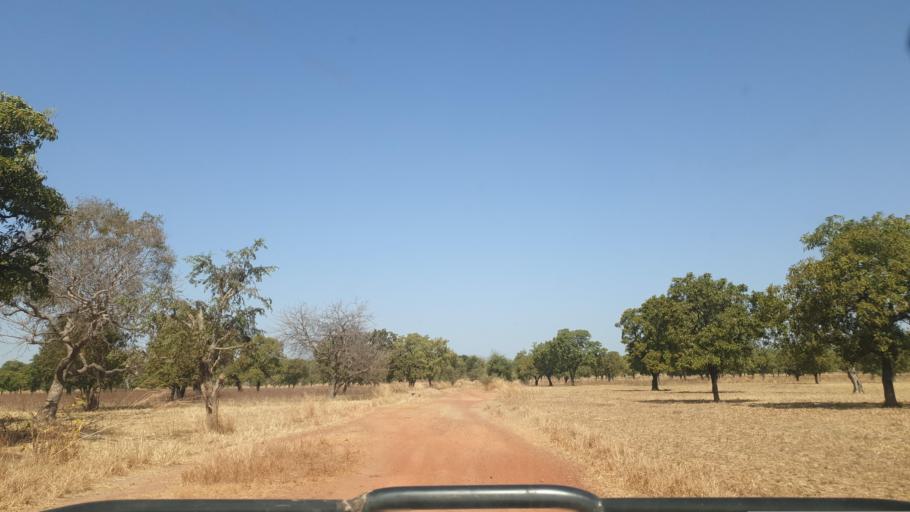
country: ML
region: Koulikoro
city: Dioila
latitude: 11.9009
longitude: -6.9818
